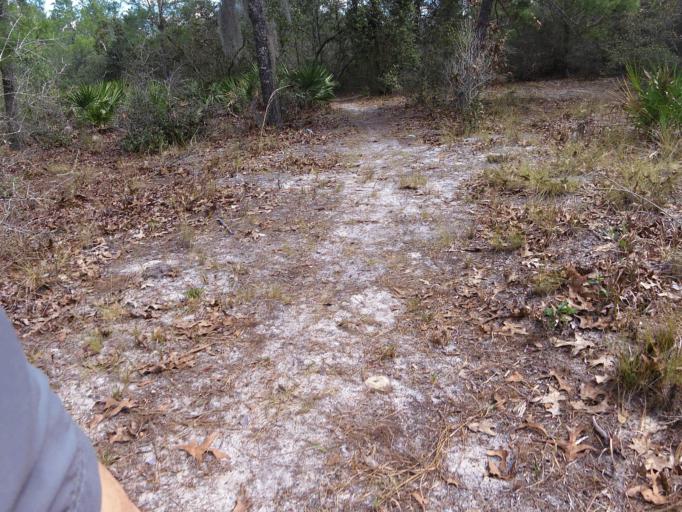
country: US
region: Florida
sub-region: Putnam County
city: Interlachen
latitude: 29.7627
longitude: -81.8537
